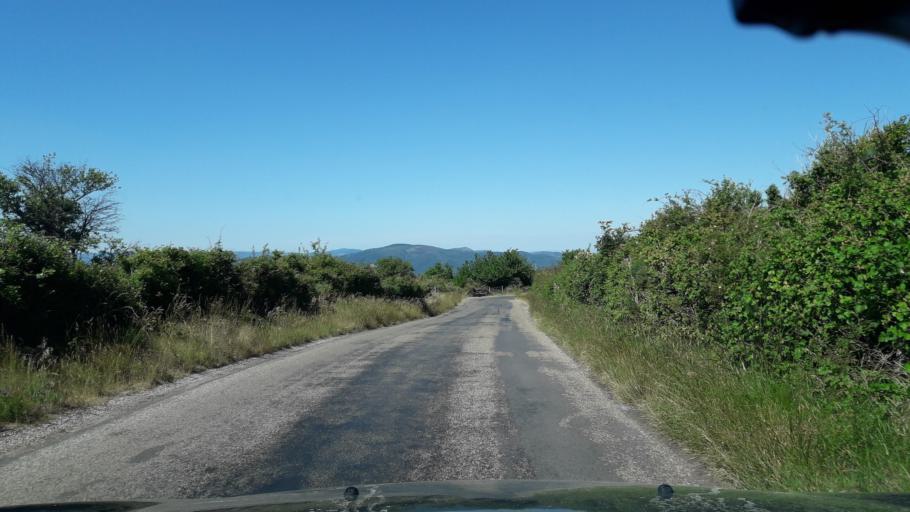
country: FR
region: Rhone-Alpes
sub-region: Departement de l'Ardeche
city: Saint-Priest
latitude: 44.6918
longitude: 4.5751
